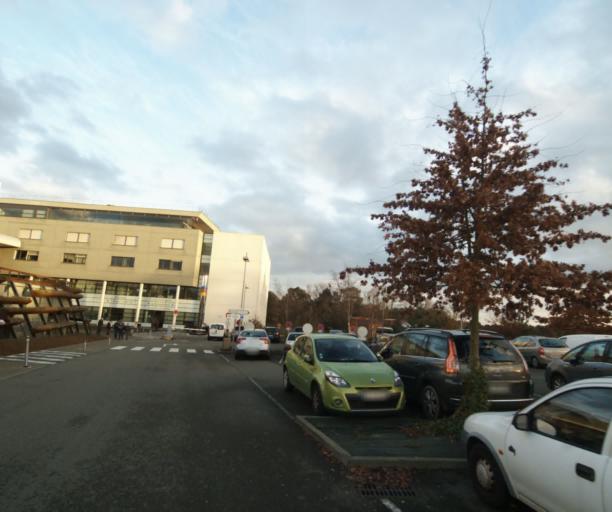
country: FR
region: Pays de la Loire
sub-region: Departement de la Sarthe
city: Le Mans
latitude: 47.9650
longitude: 0.2246
